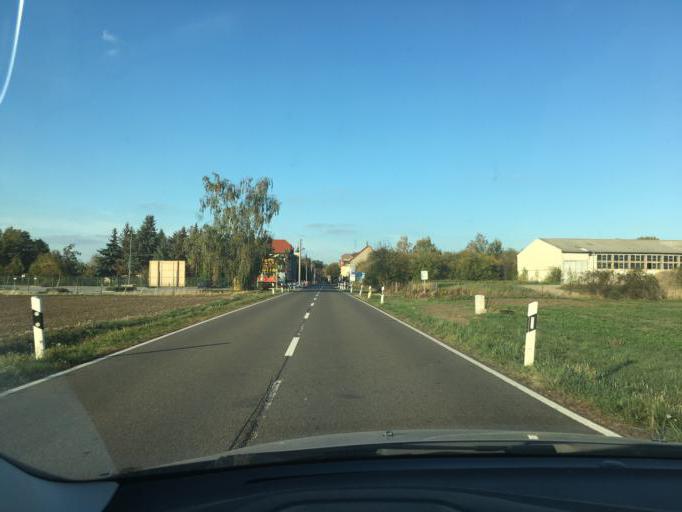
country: DE
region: Saxony-Anhalt
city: Lutzen
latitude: 51.2488
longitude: 12.1394
